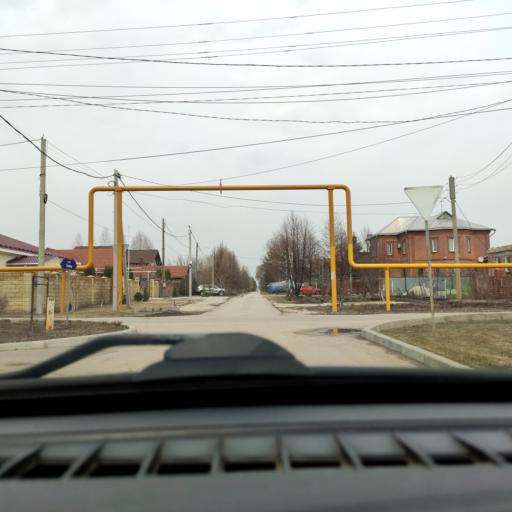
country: RU
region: Samara
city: Podstepki
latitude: 53.5172
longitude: 49.1775
